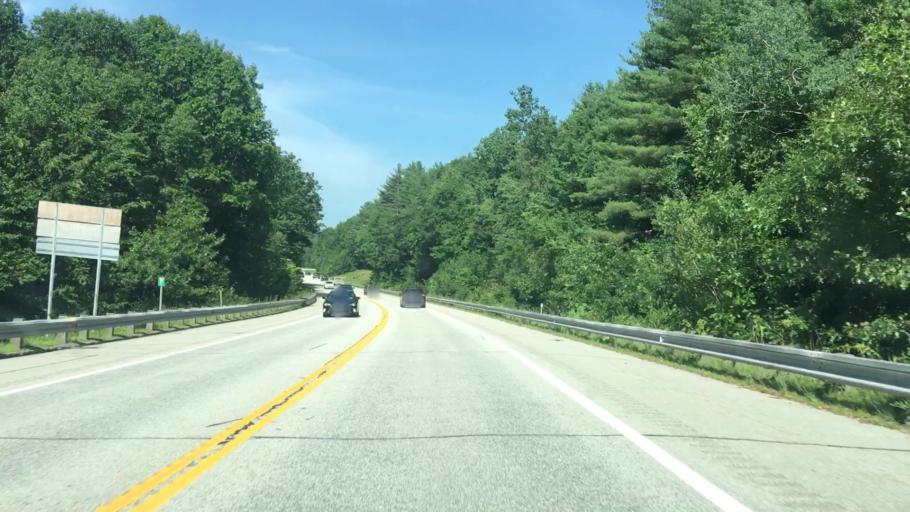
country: US
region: New Hampshire
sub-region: Merrimack County
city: Henniker
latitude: 43.1855
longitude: -71.7925
